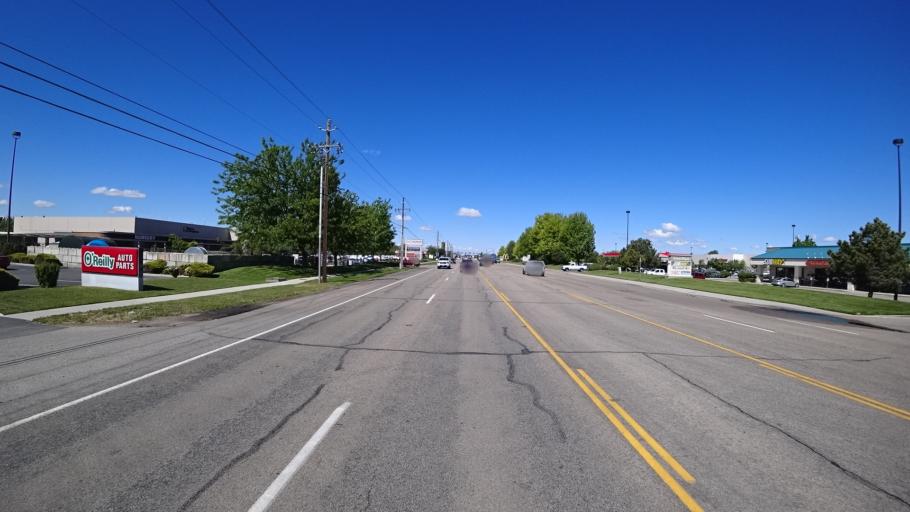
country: US
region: Idaho
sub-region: Ada County
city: Meridian
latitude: 43.6194
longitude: -116.3704
